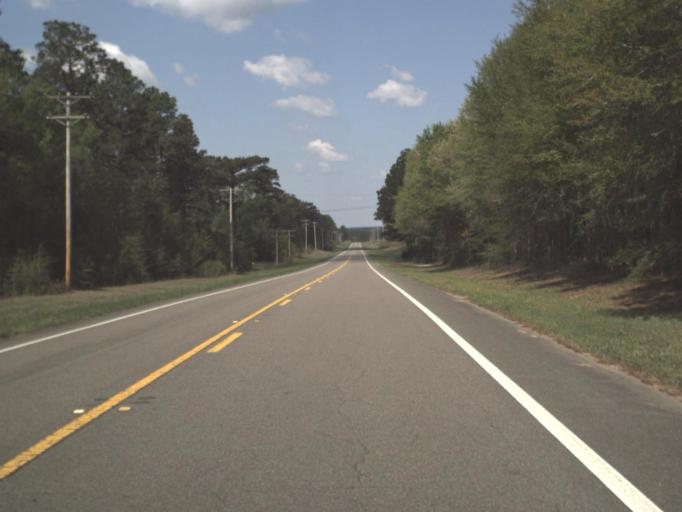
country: US
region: Florida
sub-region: Santa Rosa County
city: Point Baker
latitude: 30.8585
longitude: -86.8782
